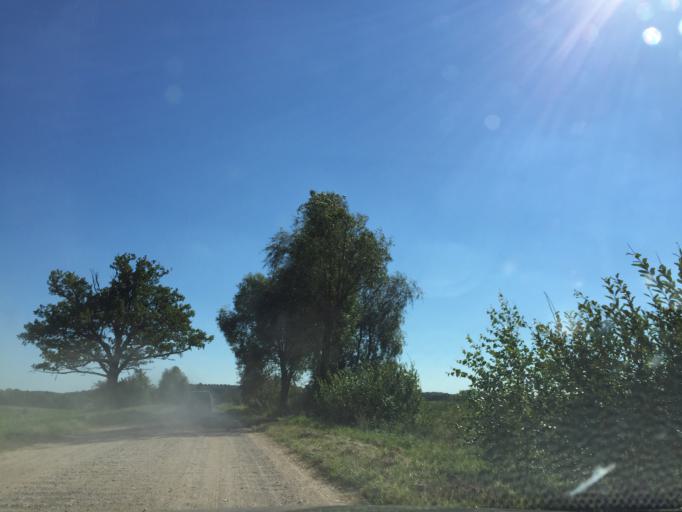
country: LT
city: Zarasai
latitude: 55.8020
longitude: 25.9482
